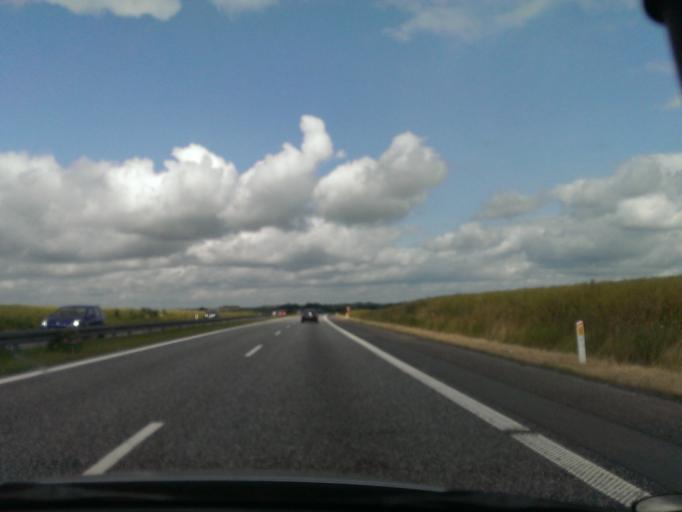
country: DK
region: Central Jutland
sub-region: Randers Kommune
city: Spentrup
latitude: 56.5309
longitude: 9.9311
